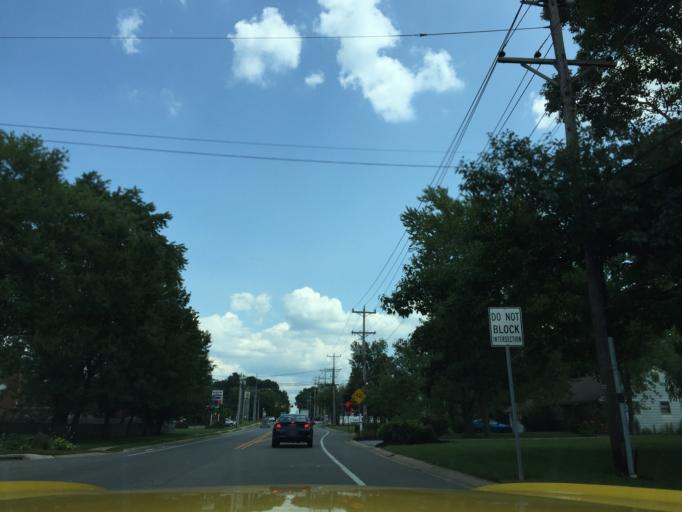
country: US
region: Delaware
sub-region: New Castle County
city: Bellefonte
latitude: 39.8095
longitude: -75.5175
